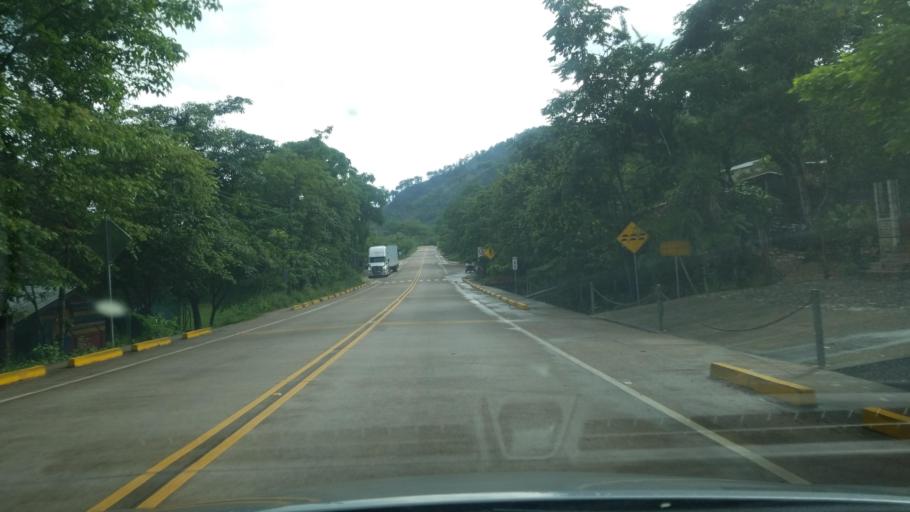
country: HN
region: Copan
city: Copan
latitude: 14.8411
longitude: -89.1746
